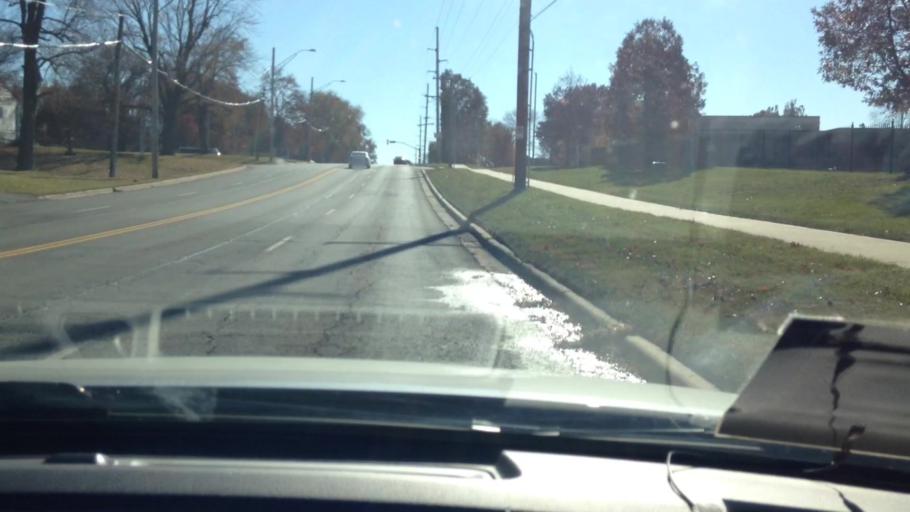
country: US
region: Missouri
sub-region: Jackson County
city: Raytown
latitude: 39.0386
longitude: -94.4480
